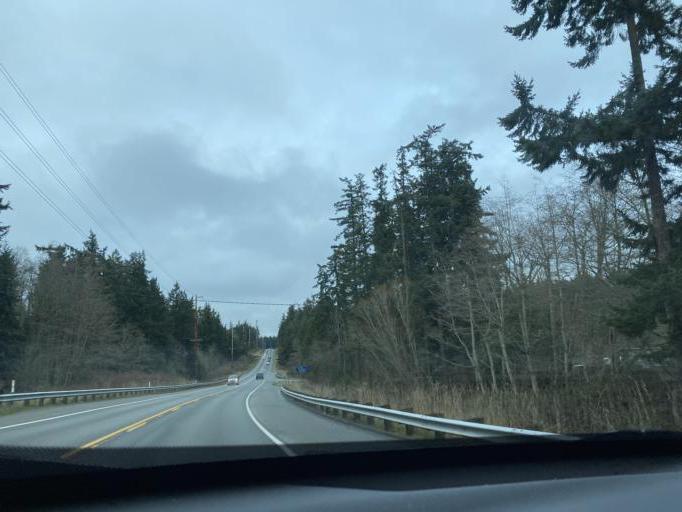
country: US
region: Washington
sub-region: Island County
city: Freeland
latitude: 48.0249
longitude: -122.5597
